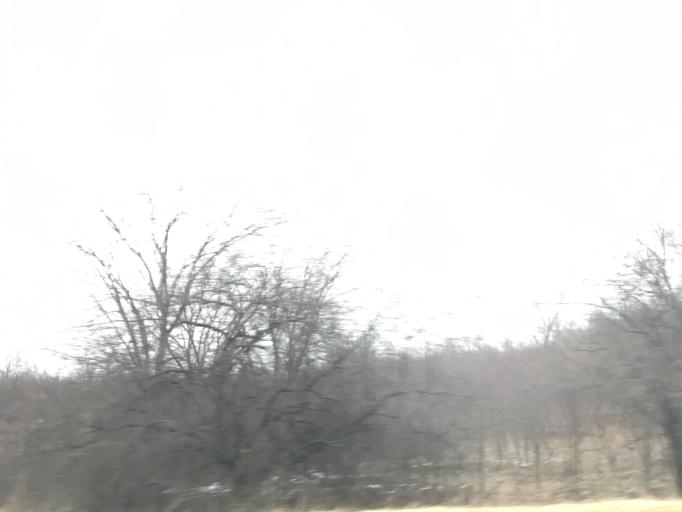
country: US
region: Illinois
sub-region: Cook County
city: Streamwood
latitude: 42.0610
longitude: -88.1655
